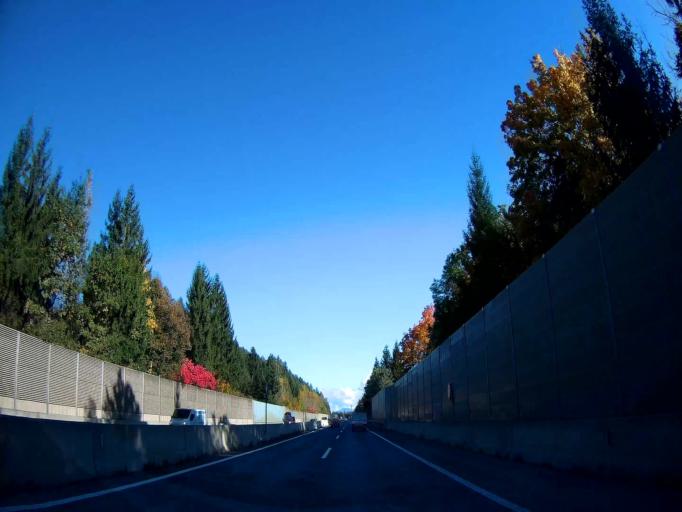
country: AT
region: Carinthia
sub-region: Politischer Bezirk Klagenfurt Land
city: Maria Worth
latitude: 46.6377
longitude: 14.1578
